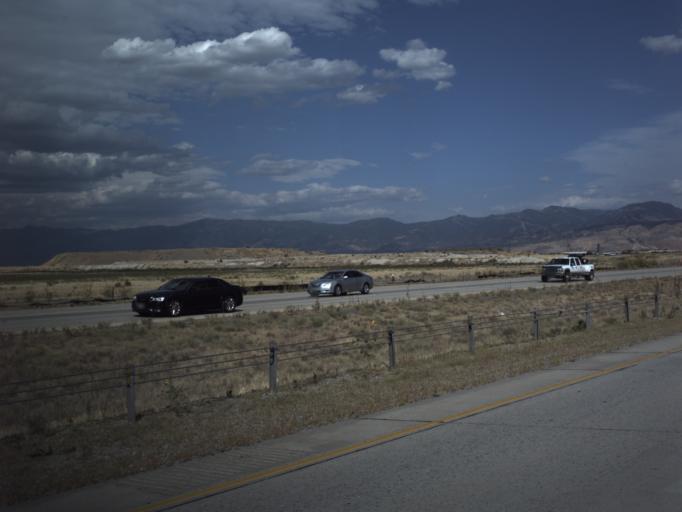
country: US
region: Utah
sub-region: Salt Lake County
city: Magna
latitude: 40.7708
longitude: -112.0718
